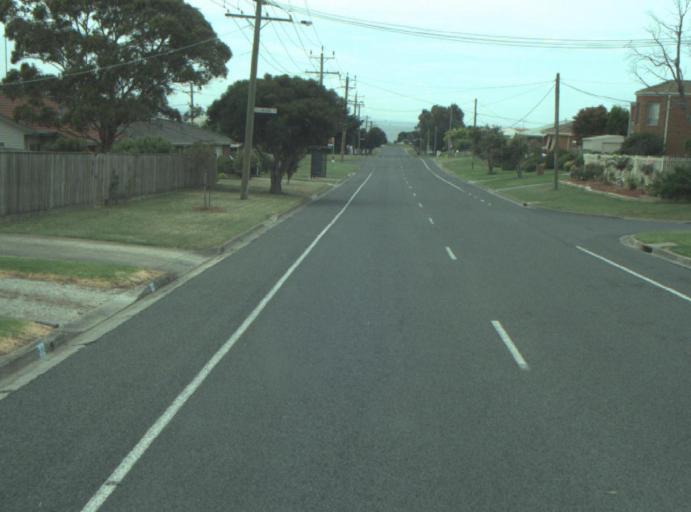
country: AU
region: Victoria
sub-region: Greater Geelong
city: Clifton Springs
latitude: -38.1461
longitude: 144.5760
